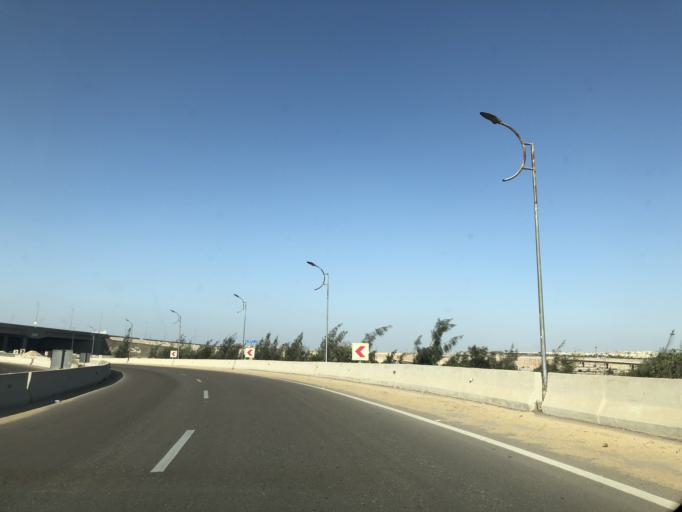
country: EG
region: Al Jizah
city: Awsim
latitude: 30.0734
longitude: 30.9260
